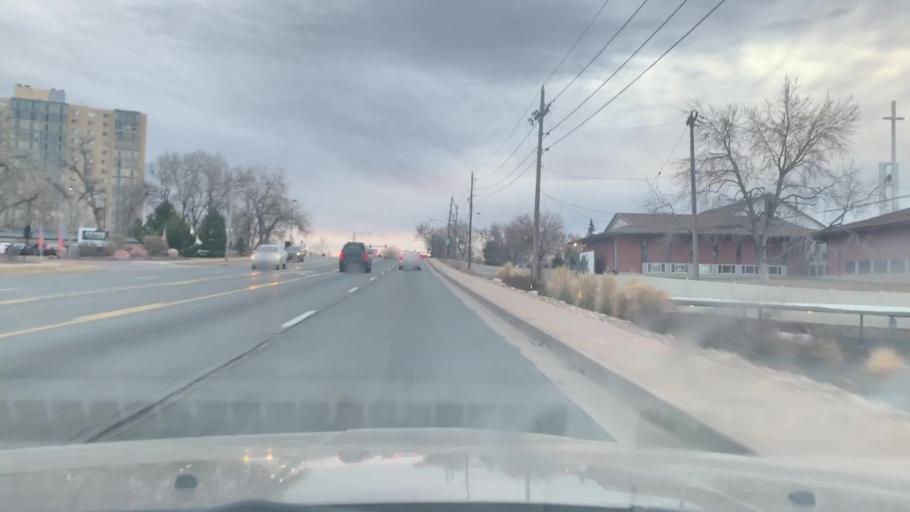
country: US
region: Colorado
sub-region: Arapahoe County
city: Glendale
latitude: 39.6973
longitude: -104.9003
